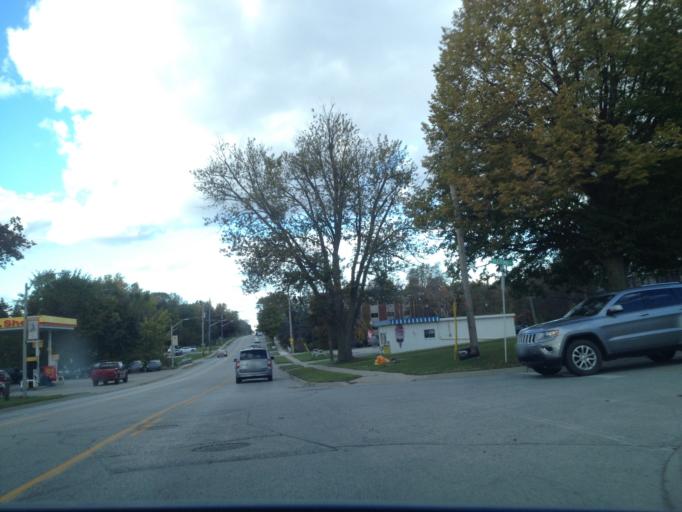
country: CA
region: Ontario
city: Amherstburg
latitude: 42.0402
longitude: -82.7395
